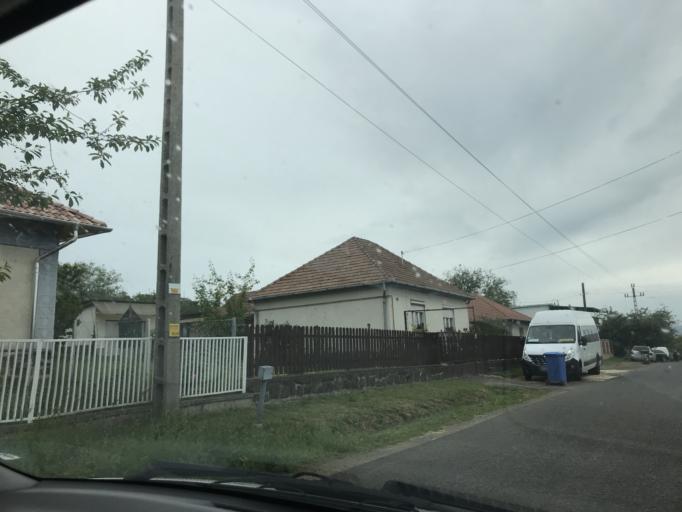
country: HU
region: Nograd
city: Batonyterenye
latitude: 47.9705
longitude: 19.8200
